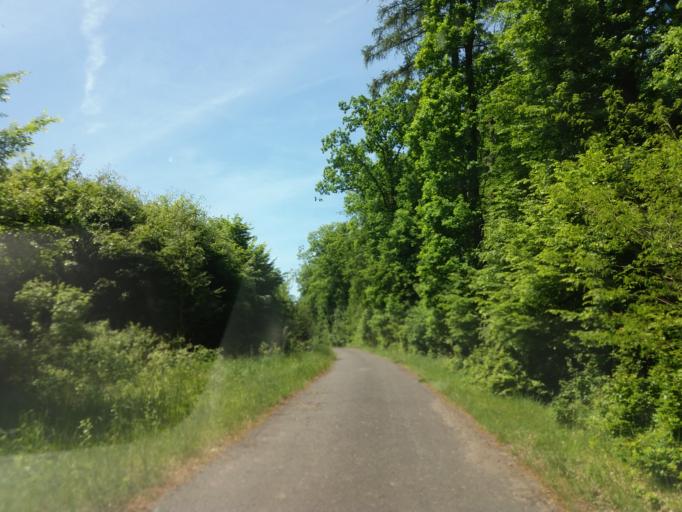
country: PL
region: West Pomeranian Voivodeship
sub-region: Powiat stargardzki
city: Dobrzany
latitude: 53.3507
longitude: 15.4647
